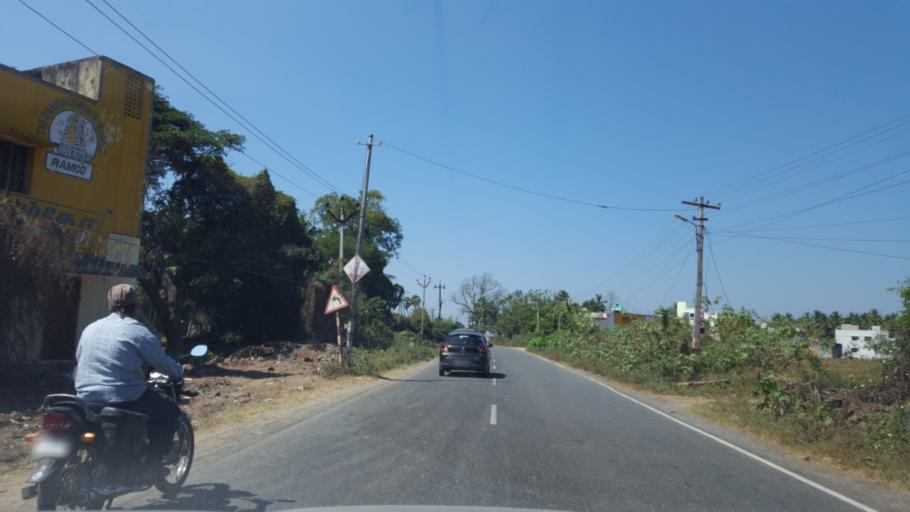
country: IN
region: Tamil Nadu
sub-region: Kancheepuram
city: Chengalpattu
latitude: 12.7136
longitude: 79.9594
